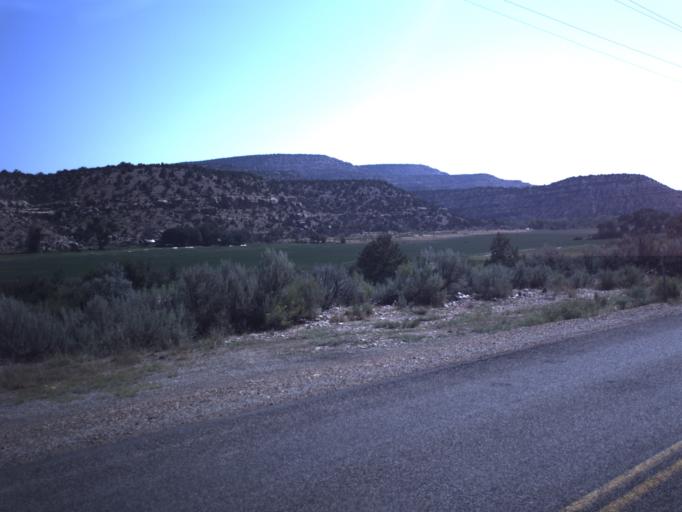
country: US
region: Utah
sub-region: Duchesne County
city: Duchesne
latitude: 40.2948
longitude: -110.5094
